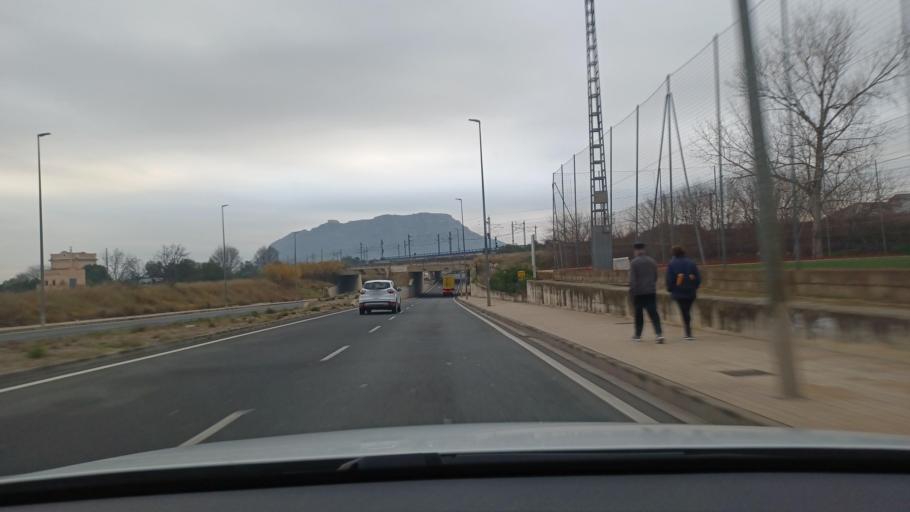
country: ES
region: Valencia
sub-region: Provincia de Valencia
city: Xativa
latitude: 38.9970
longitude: -0.5175
